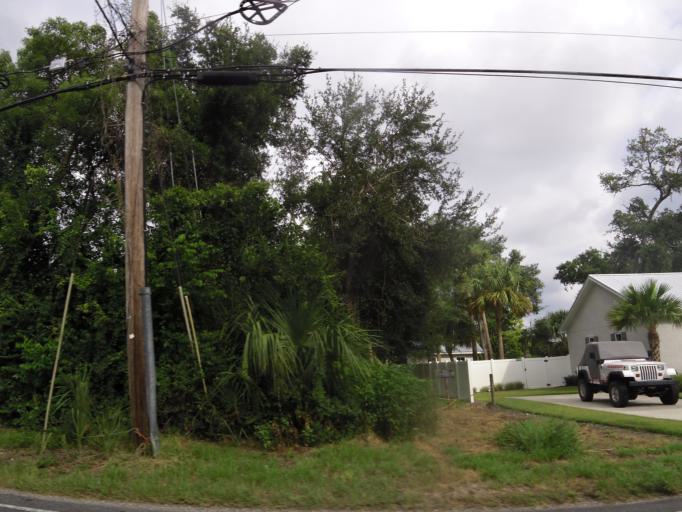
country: US
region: Georgia
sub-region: Glynn County
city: Saint Simons Island
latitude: 31.1438
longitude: -81.3834
